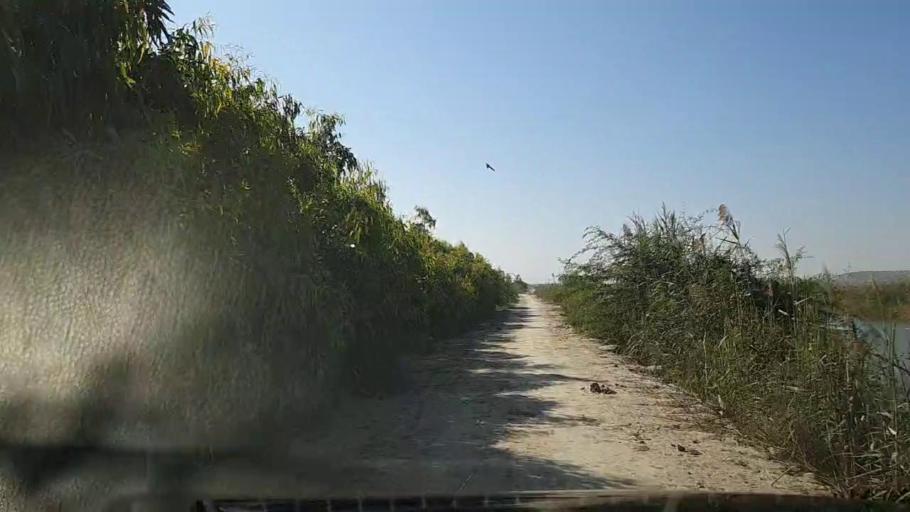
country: PK
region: Sindh
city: Thatta
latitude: 24.6914
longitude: 67.8943
